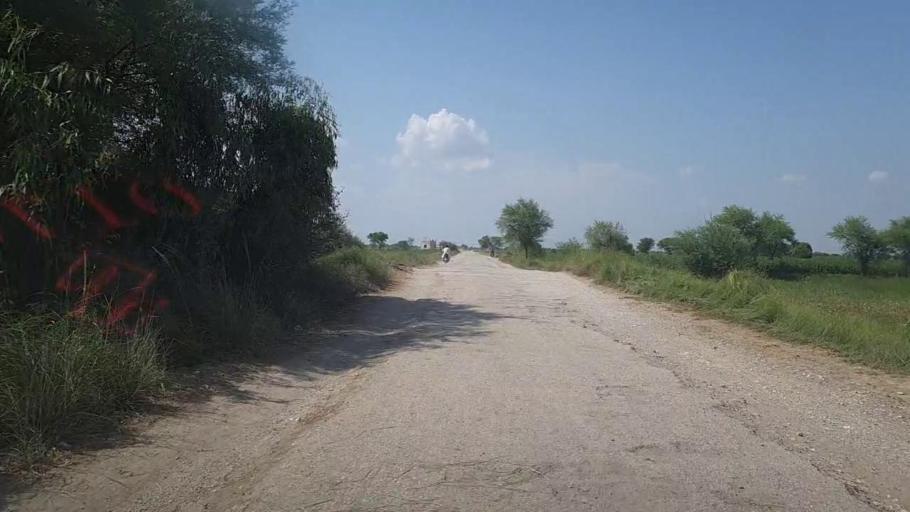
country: PK
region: Sindh
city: Khairpur
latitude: 28.0927
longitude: 69.6299
